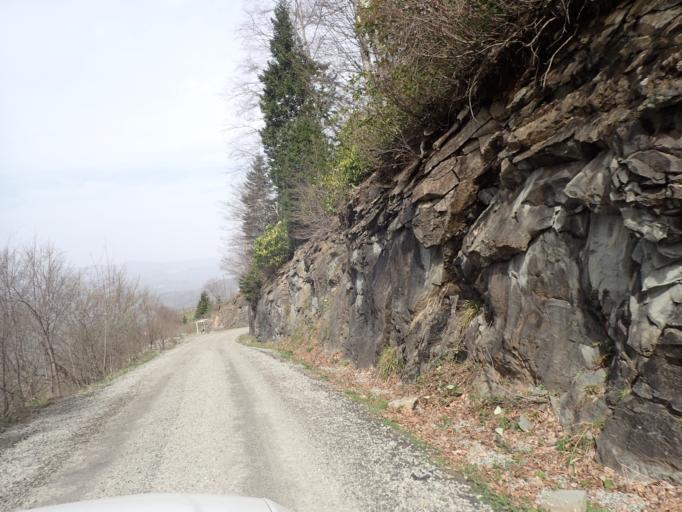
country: TR
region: Ordu
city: Kabaduz
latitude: 40.7798
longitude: 37.9004
